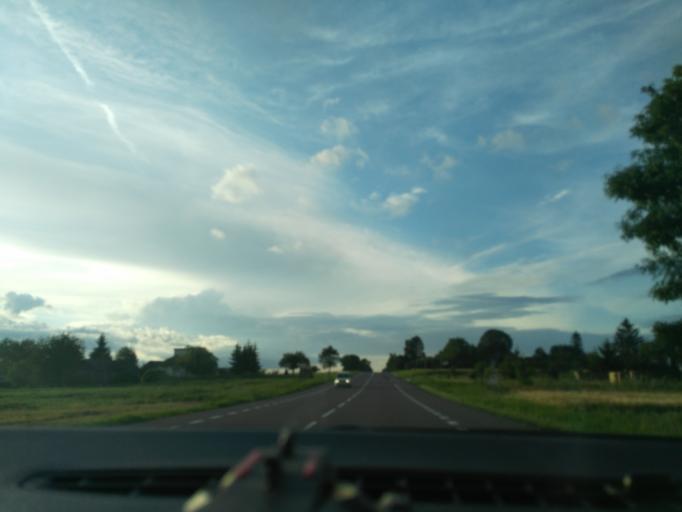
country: PL
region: Lublin Voivodeship
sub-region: Powiat lubelski
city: Niedrzwica Duza
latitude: 51.0668
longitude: 22.3799
